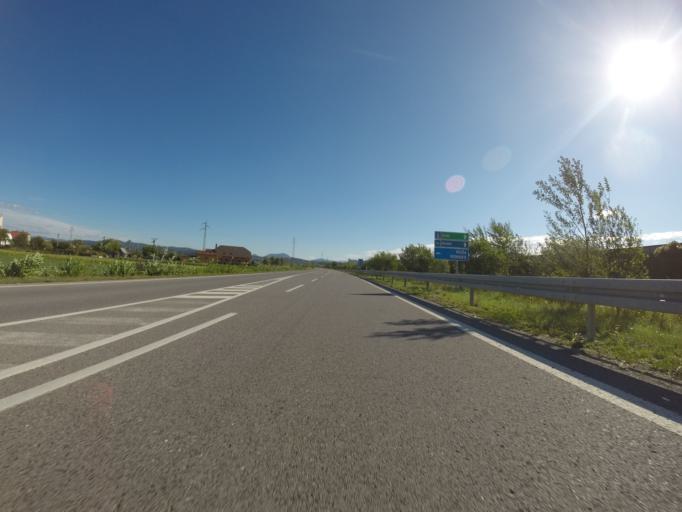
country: SK
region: Nitriansky
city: Puchov
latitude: 49.0480
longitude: 18.3131
